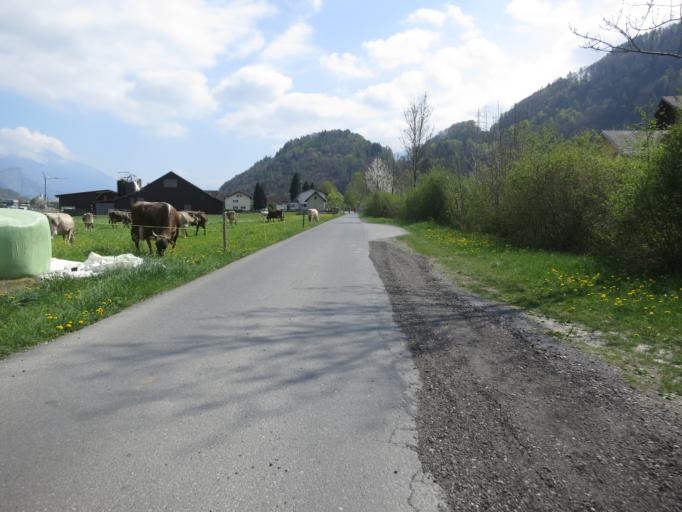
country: CH
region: Saint Gallen
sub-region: Wahlkreis Sarganserland
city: Sargans
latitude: 47.0584
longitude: 9.4002
